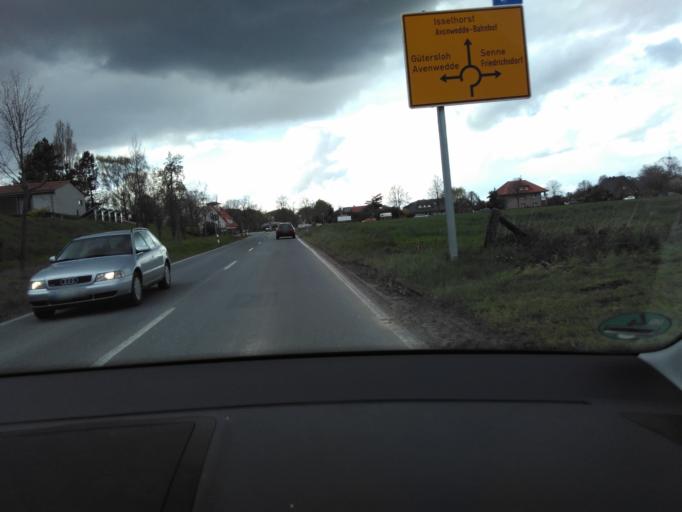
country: DE
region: North Rhine-Westphalia
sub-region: Regierungsbezirk Detmold
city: Verl
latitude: 51.9172
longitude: 8.4538
